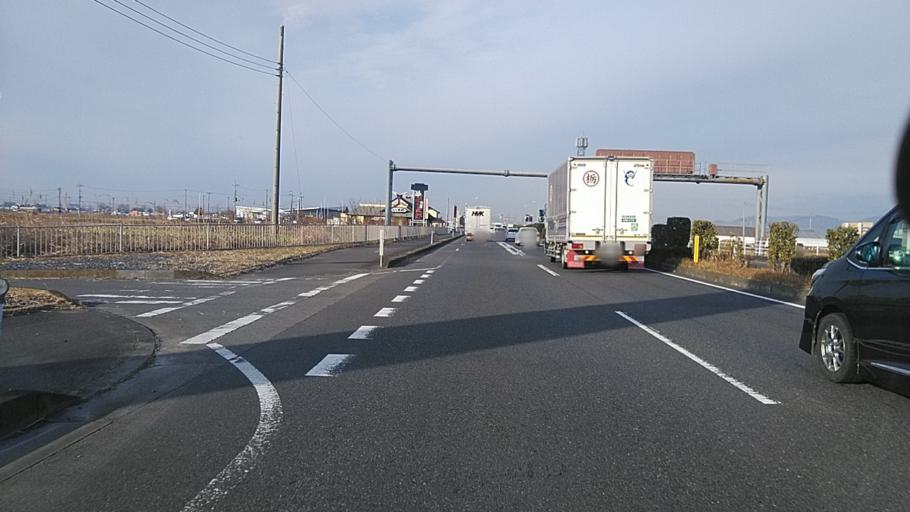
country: JP
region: Tochigi
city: Oyama
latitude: 36.3087
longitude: 139.7648
